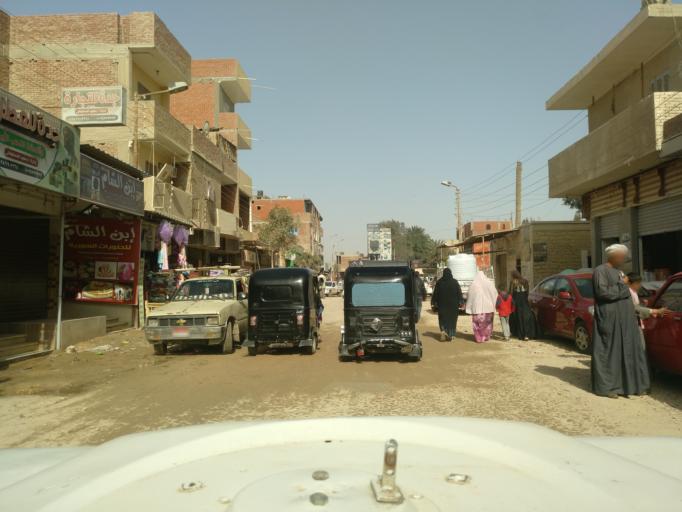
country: EG
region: Al Buhayrah
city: Beheira
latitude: 30.3763
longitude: 30.3485
